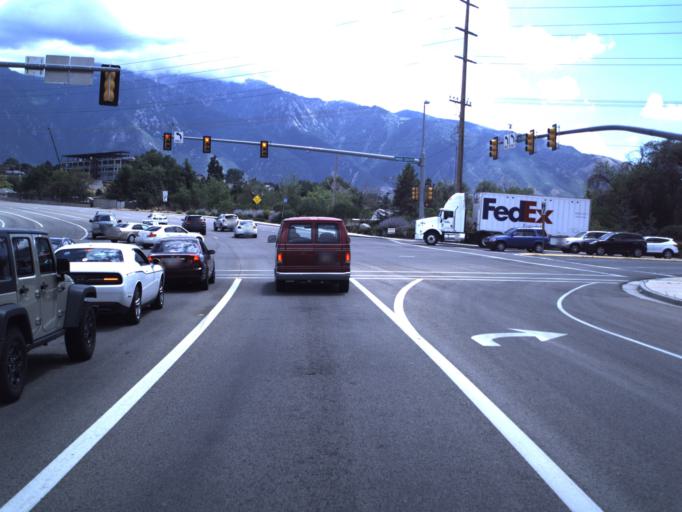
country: US
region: Utah
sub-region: Salt Lake County
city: Sandy Hills
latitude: 40.5813
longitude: -111.8619
